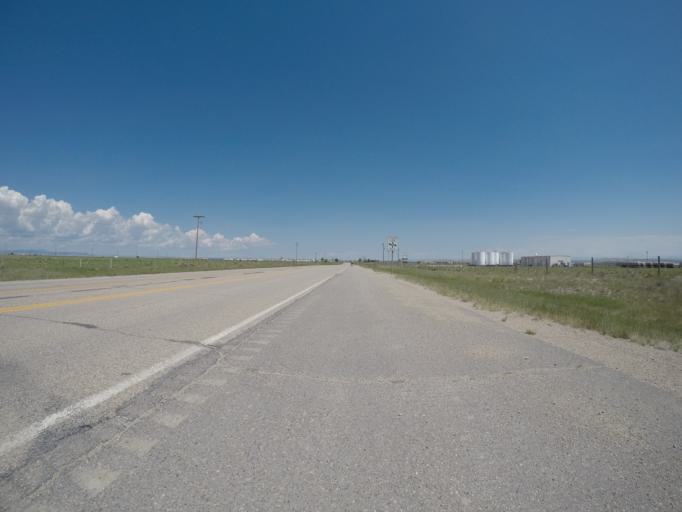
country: US
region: Wyoming
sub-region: Sublette County
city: Marbleton
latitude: 42.5062
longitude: -110.1049
